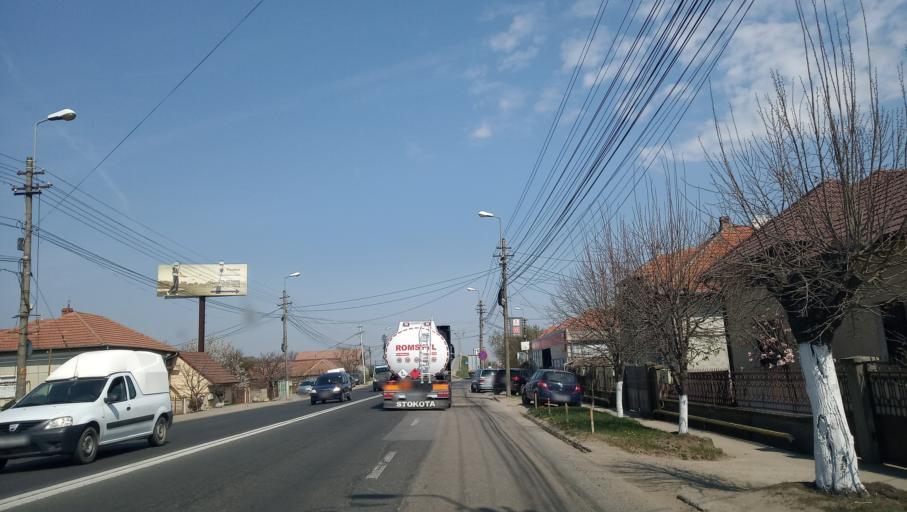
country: RO
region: Alba
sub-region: Municipiul Alba Iulia
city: Alba Iulia
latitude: 46.0477
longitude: 23.5669
